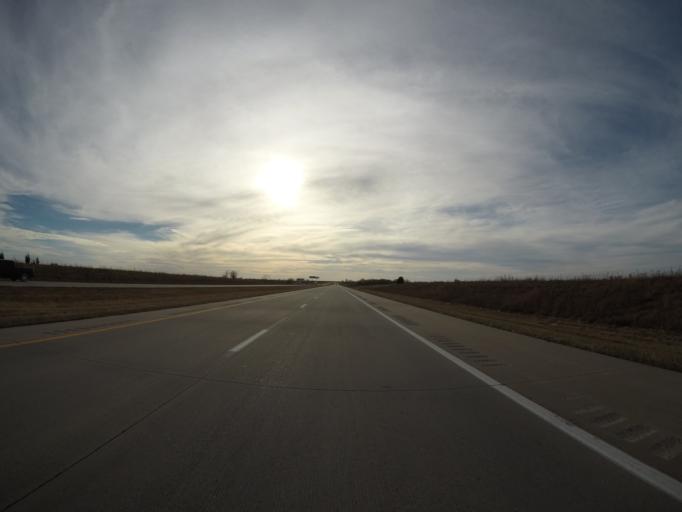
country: US
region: Kansas
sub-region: Franklin County
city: Wellsville
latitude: 38.6902
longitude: -95.1127
